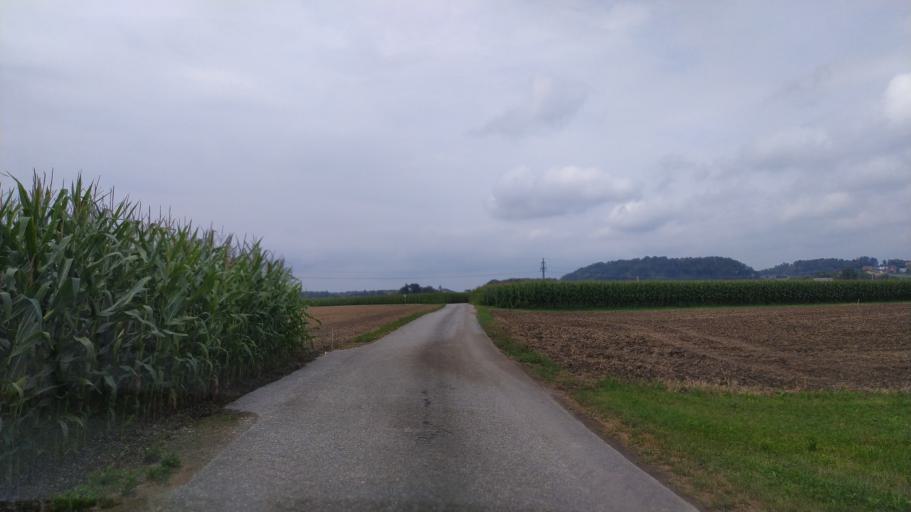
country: AT
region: Upper Austria
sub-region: Politischer Bezirk Perg
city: Bad Kreuzen
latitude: 48.2014
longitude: 14.7642
